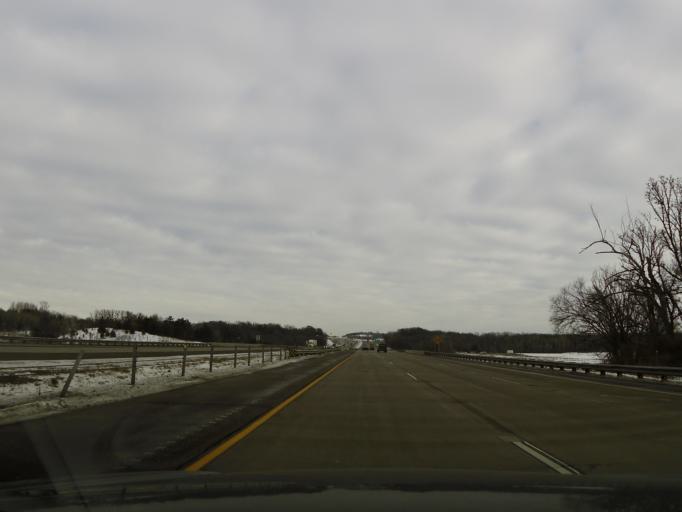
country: US
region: Wisconsin
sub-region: Saint Croix County
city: Hudson
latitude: 44.9640
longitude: -92.6967
